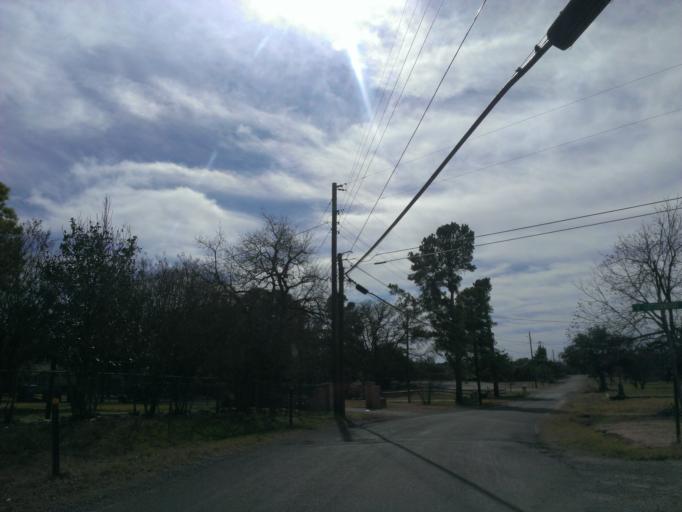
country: US
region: Texas
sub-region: Burnet County
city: Granite Shoals
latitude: 30.5821
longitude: -98.3876
